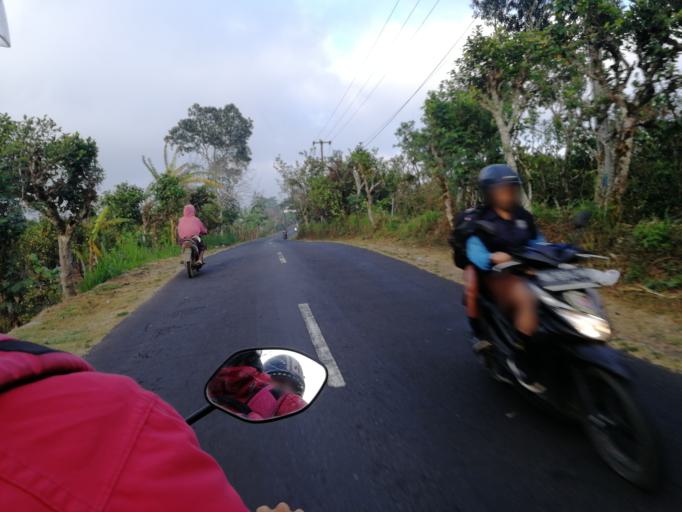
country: ID
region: Bali
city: Banjar Kedisan
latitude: -8.2236
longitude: 115.2578
